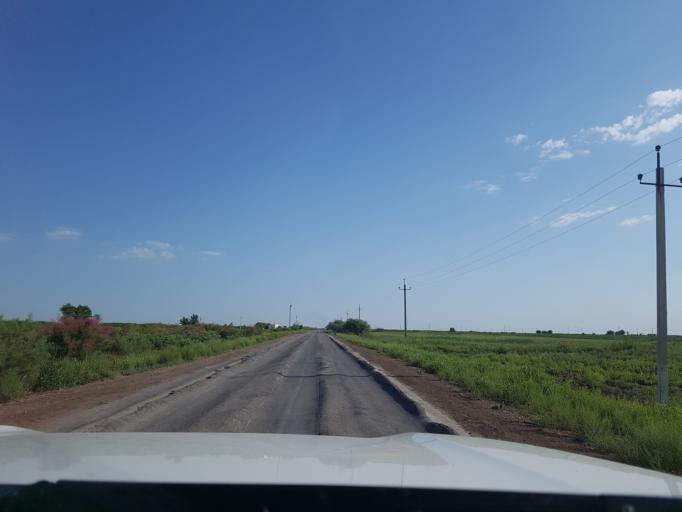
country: TM
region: Dasoguz
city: Koeneuergench
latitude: 41.8747
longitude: 58.7061
